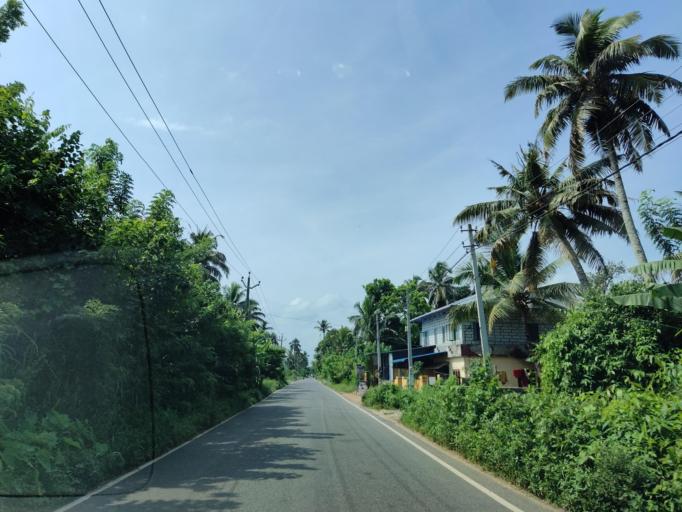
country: IN
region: Kerala
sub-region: Pattanamtitta
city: Tiruvalla
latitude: 9.3410
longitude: 76.4678
